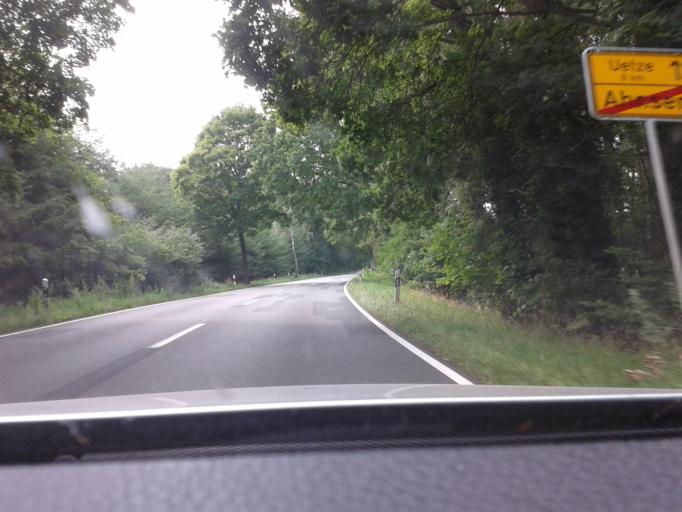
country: DE
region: Lower Saxony
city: Meinersen
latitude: 52.4840
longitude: 10.3243
